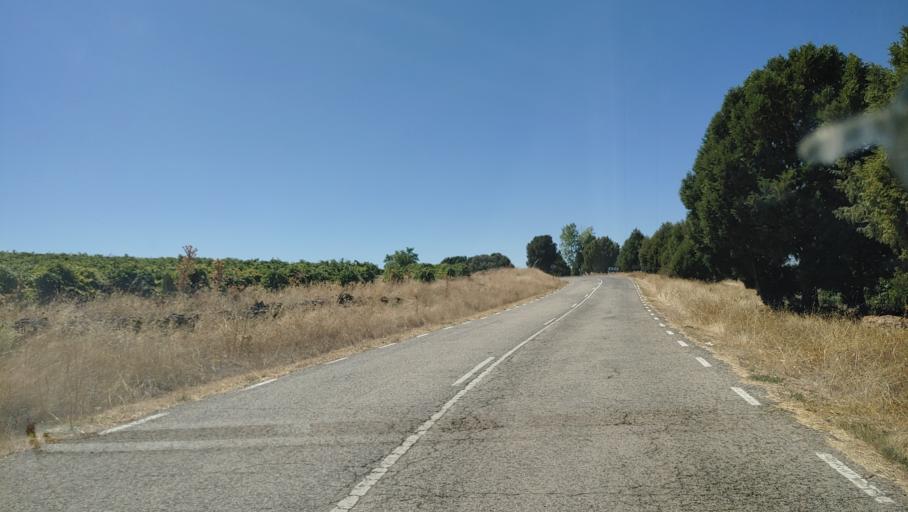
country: ES
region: Castille-La Mancha
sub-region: Provincia de Albacete
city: Ossa de Montiel
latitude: 38.8965
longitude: -2.7648
